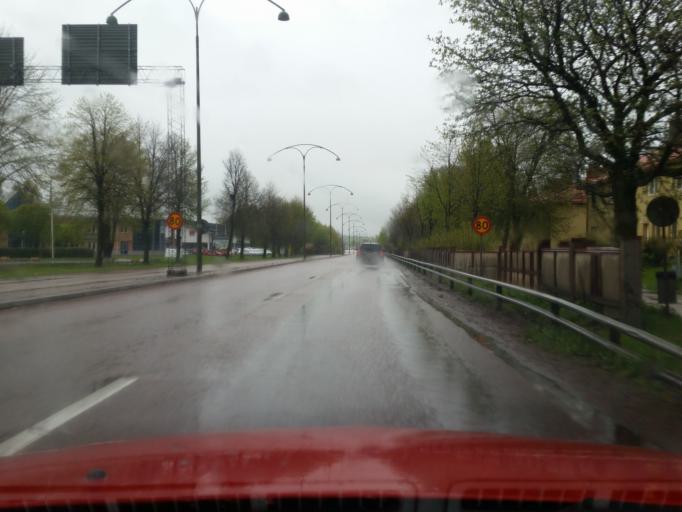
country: SE
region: Dalarna
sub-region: Borlange Kommun
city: Borlaenge
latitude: 60.4780
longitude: 15.4377
